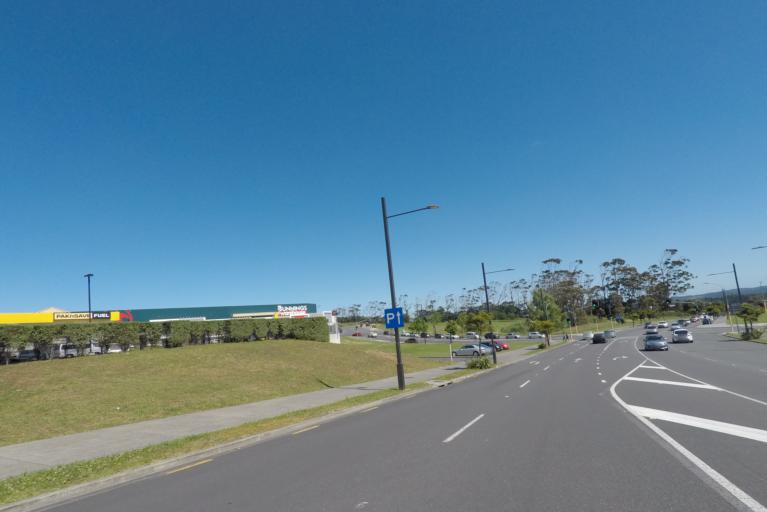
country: NZ
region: Auckland
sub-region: Auckland
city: Rosebank
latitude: -36.8200
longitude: 174.6088
